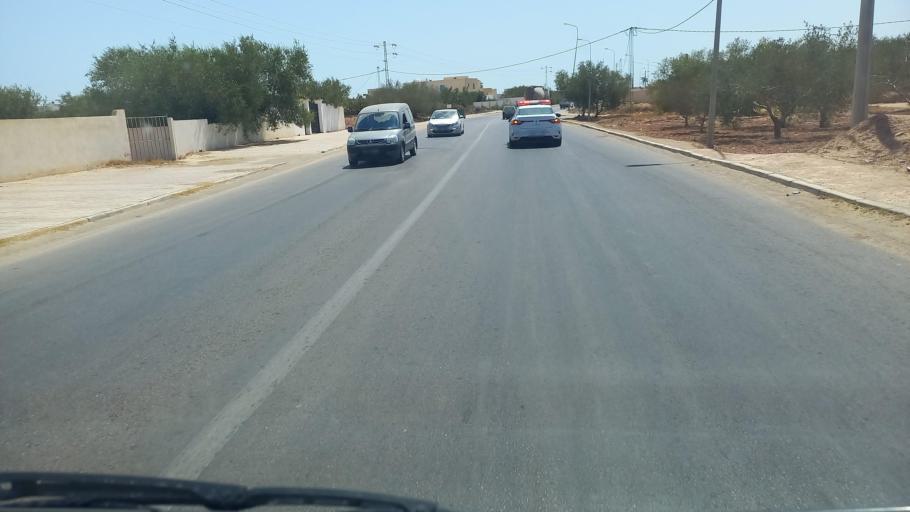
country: TN
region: Madanin
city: Houmt Souk
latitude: 33.7808
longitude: 10.8899
